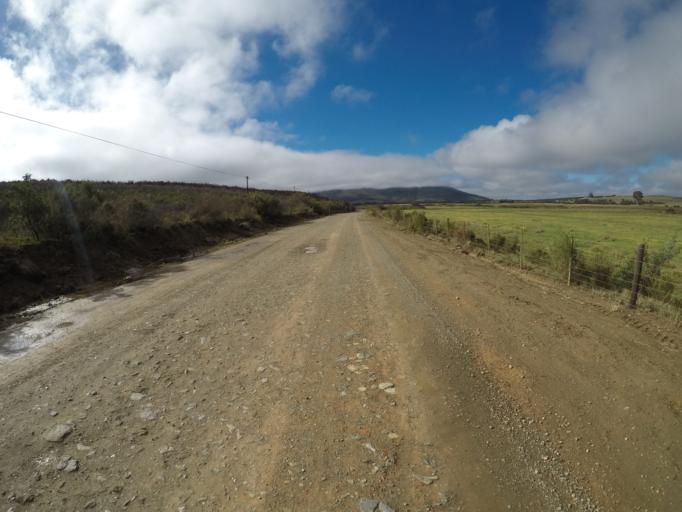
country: ZA
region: Western Cape
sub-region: Cape Winelands District Municipality
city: Ashton
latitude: -34.1235
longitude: 19.8292
